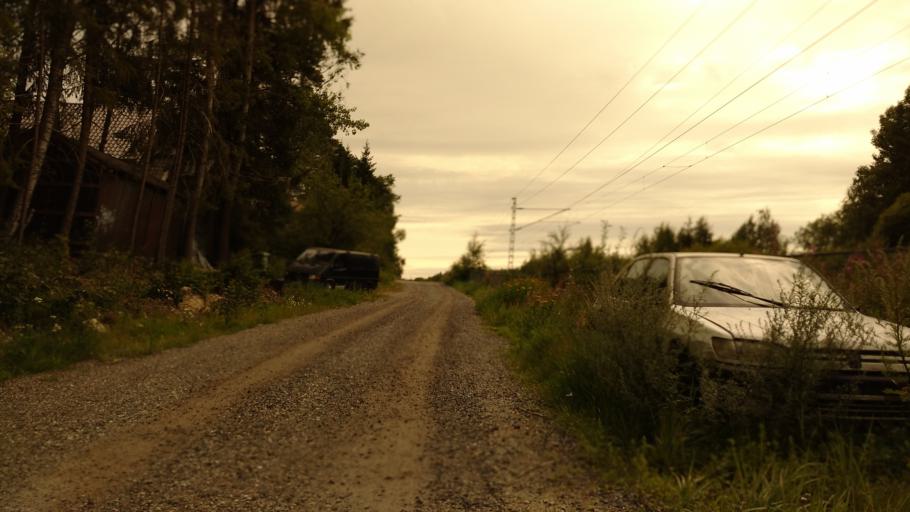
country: FI
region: Varsinais-Suomi
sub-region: Turku
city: Kaarina
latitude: 60.4435
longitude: 22.4293
